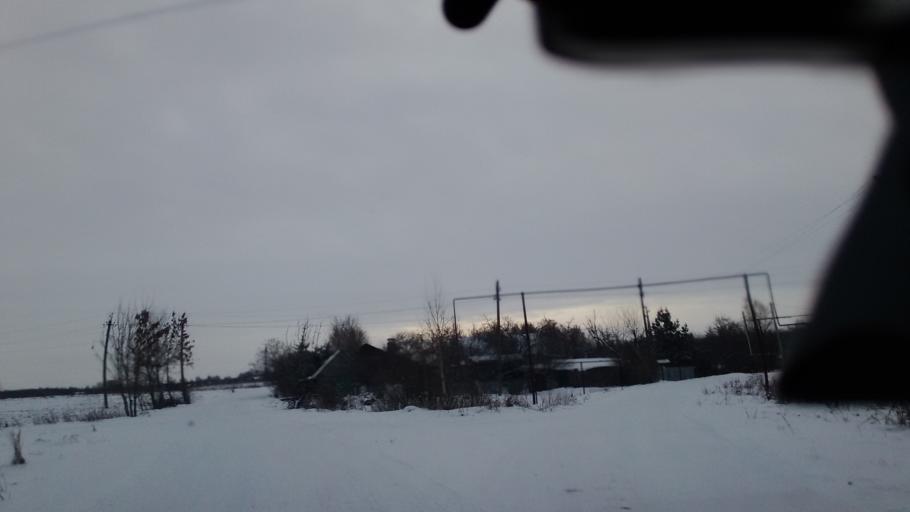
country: RU
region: Tula
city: Bogoroditsk
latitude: 53.7515
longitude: 38.1061
